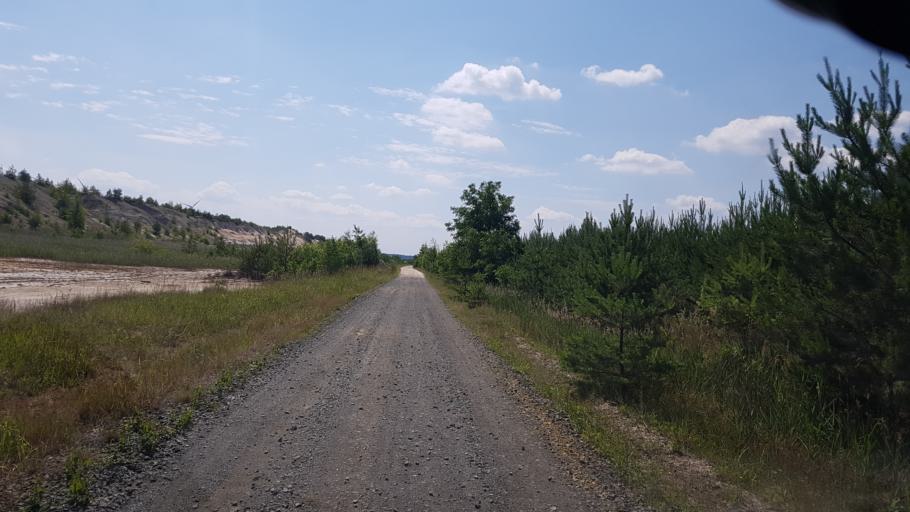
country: DE
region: Brandenburg
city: Sallgast
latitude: 51.5734
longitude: 13.8032
